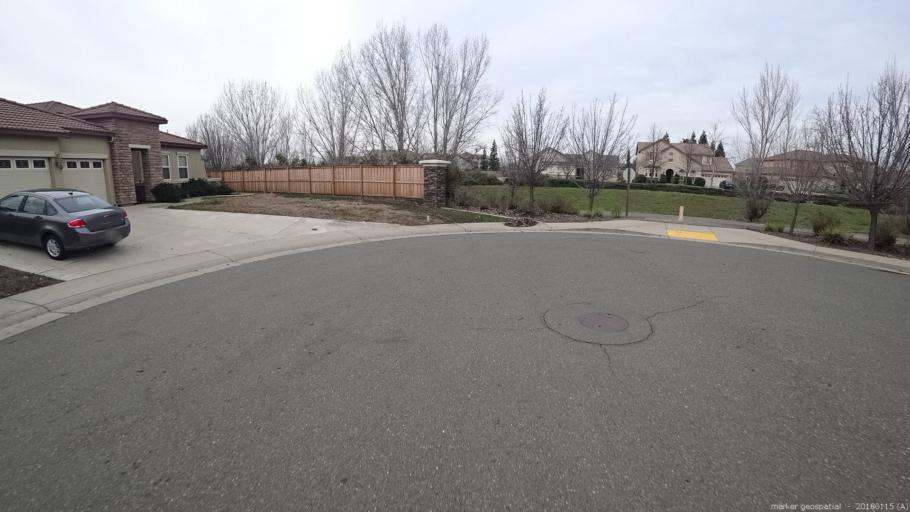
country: US
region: California
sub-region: Sacramento County
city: Rancho Cordova
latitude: 38.5762
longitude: -121.2743
